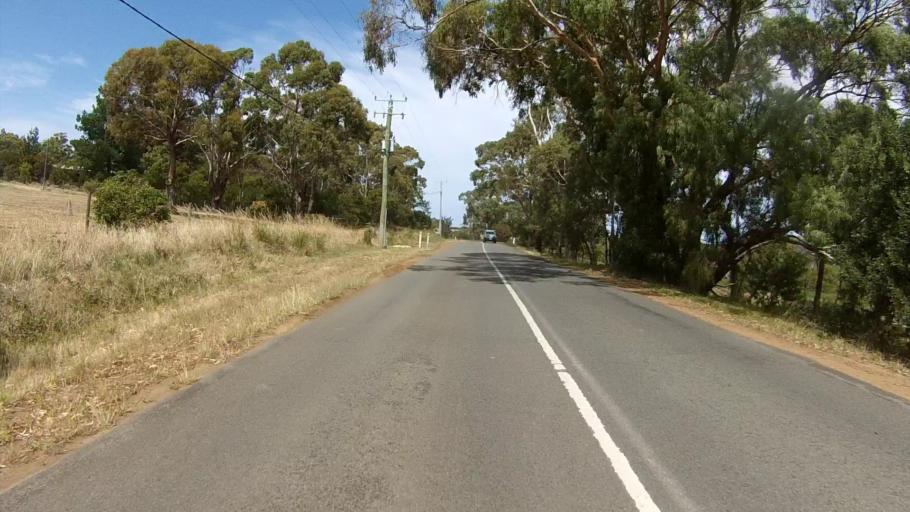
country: AU
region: Tasmania
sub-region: Kingborough
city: Taroona
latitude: -43.0157
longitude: 147.4159
